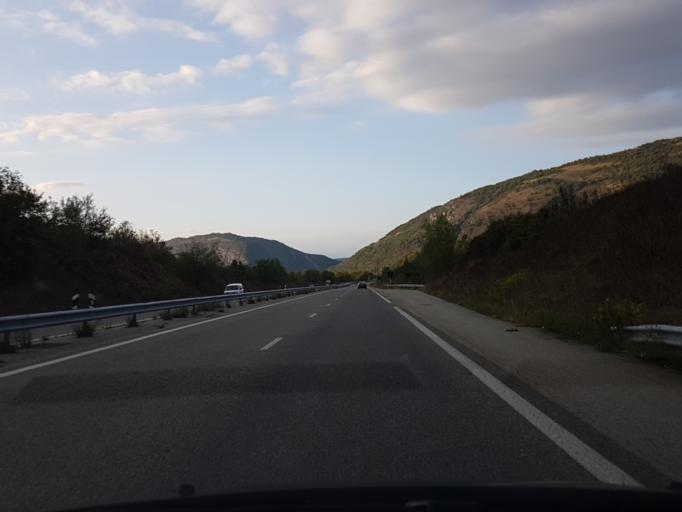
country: FR
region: Midi-Pyrenees
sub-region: Departement de l'Ariege
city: Montgaillard
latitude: 42.9385
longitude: 1.6249
